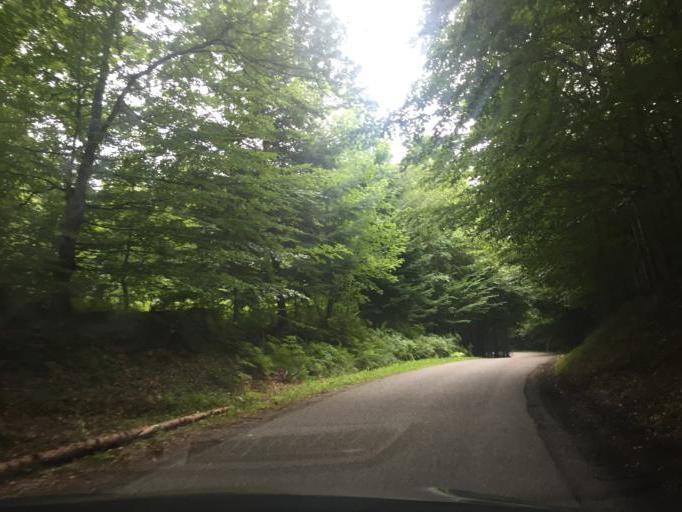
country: DK
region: South Denmark
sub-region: Assens Kommune
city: Tommerup Stationsby
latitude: 55.3728
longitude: 10.2208
